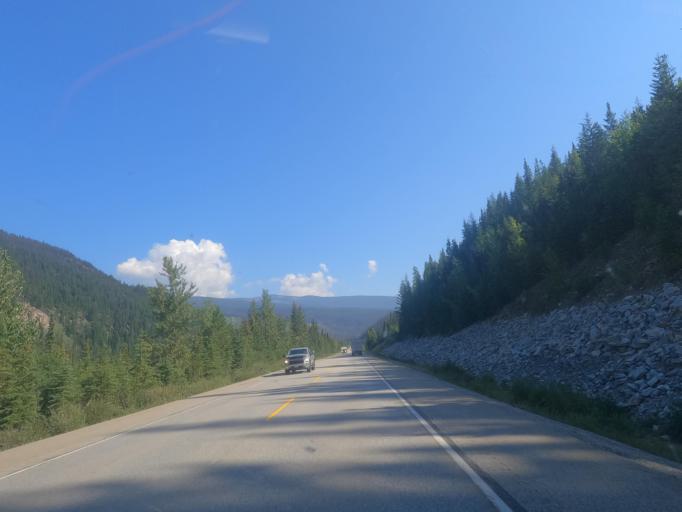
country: CA
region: Alberta
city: Jasper Park Lodge
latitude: 52.8761
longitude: -118.4964
